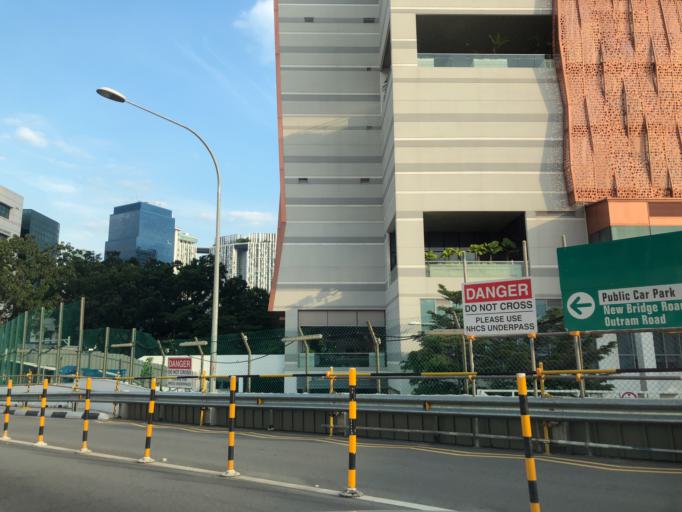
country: SG
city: Singapore
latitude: 1.2790
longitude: 103.8356
